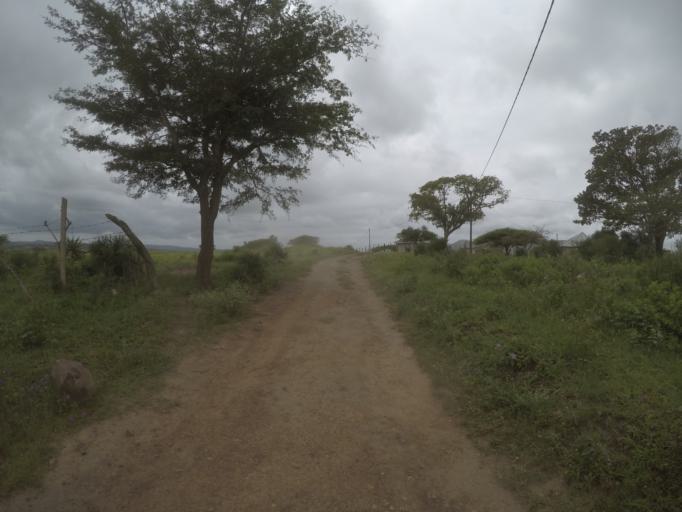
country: ZA
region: KwaZulu-Natal
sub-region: uThungulu District Municipality
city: Empangeni
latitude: -28.5967
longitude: 31.8502
